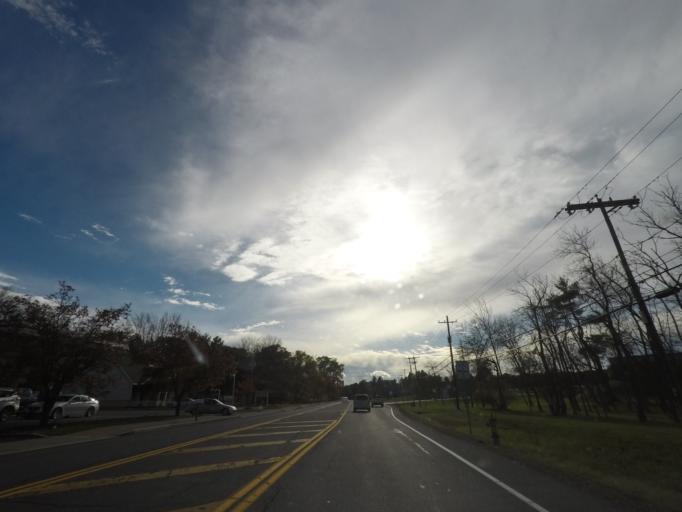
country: US
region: New York
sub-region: Albany County
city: Delmar
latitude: 42.6398
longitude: -73.8542
